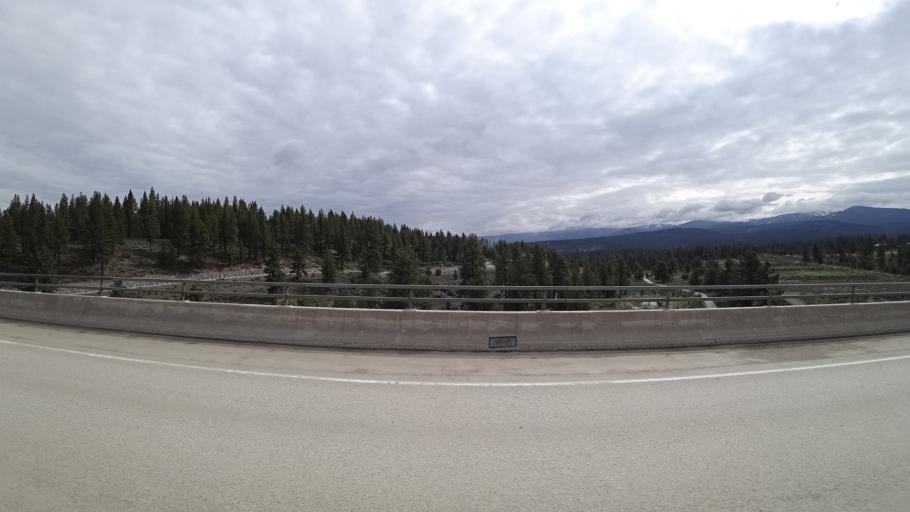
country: US
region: California
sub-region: Nevada County
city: Truckee
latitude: 39.3324
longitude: -120.1623
